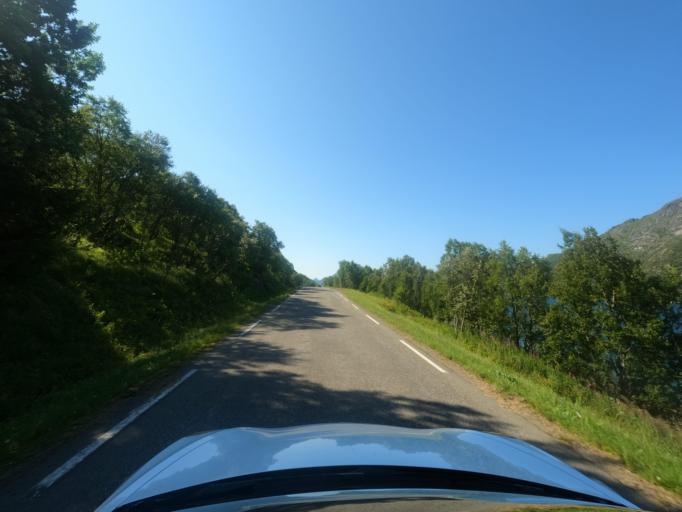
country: NO
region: Nordland
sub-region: Hadsel
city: Stokmarknes
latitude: 68.3807
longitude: 15.0878
